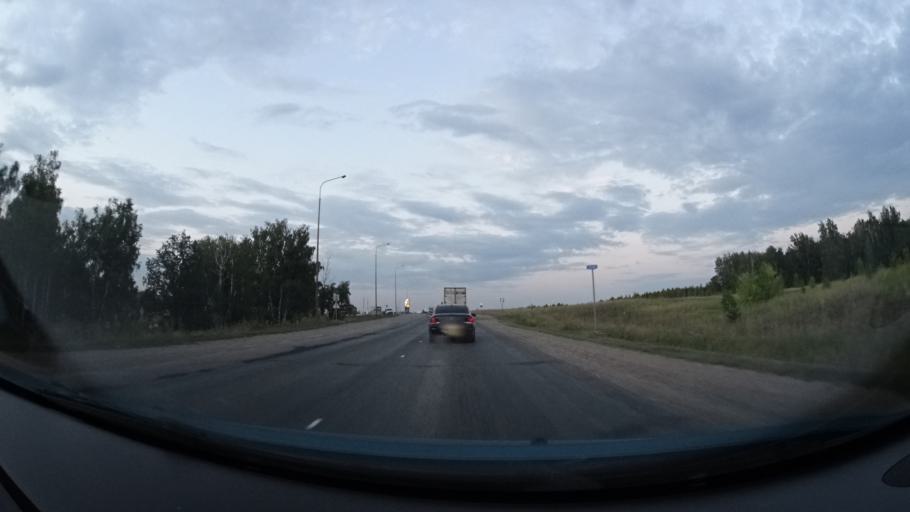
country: RU
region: Tatarstan
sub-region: Bavlinskiy Rayon
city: Bavly
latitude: 54.2692
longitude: 52.9710
